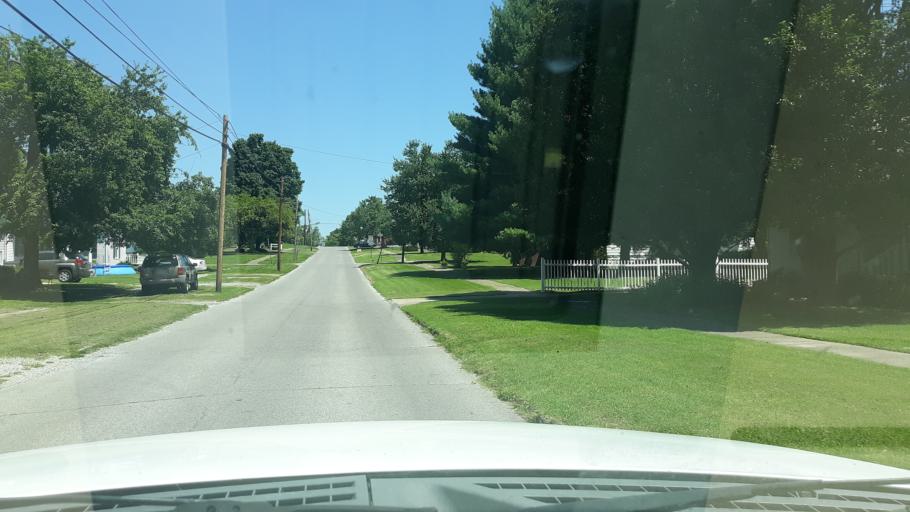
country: US
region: Illinois
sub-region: Saline County
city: Eldorado
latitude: 37.8180
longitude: -88.4361
